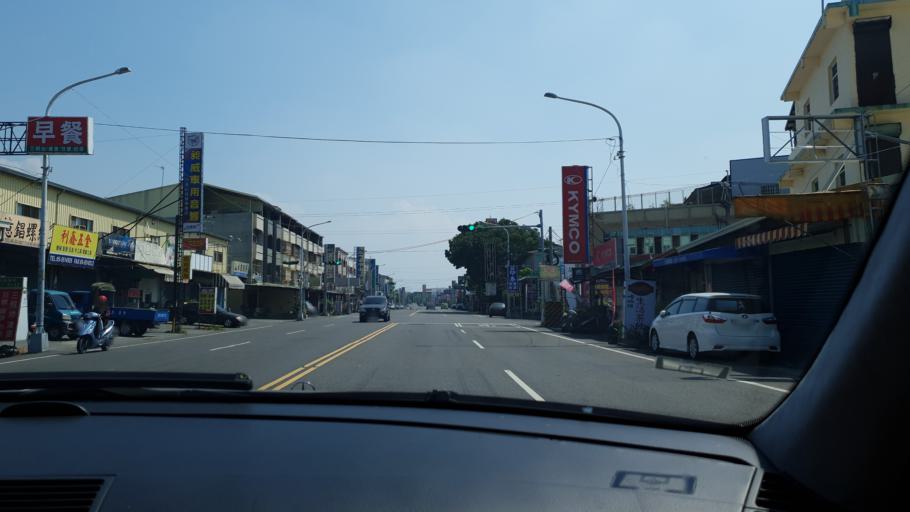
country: TW
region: Taiwan
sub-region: Yunlin
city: Douliu
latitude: 23.7229
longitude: 120.5254
